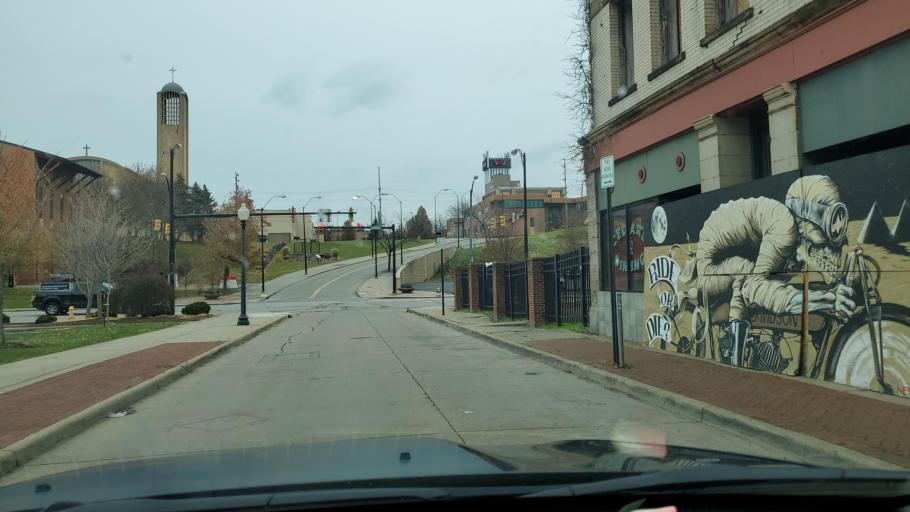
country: US
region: Ohio
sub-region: Mahoning County
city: Youngstown
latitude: 41.1016
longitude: -80.6514
